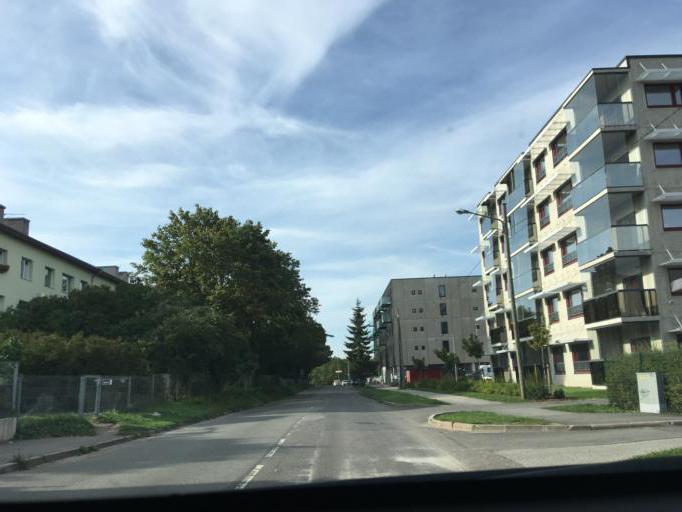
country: EE
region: Harju
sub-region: Tallinna linn
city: Tallinn
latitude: 59.4378
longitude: 24.8062
